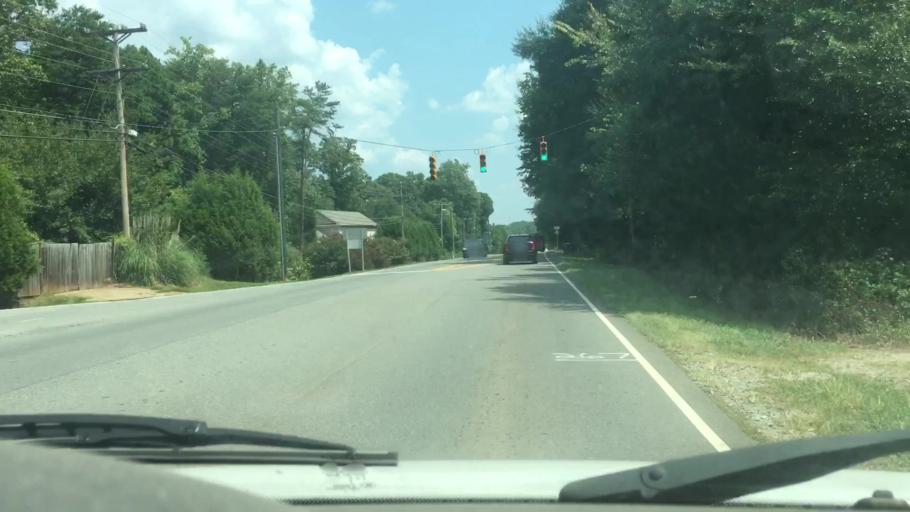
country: US
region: North Carolina
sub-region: Lincoln County
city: Lowesville
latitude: 35.4284
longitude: -80.9342
